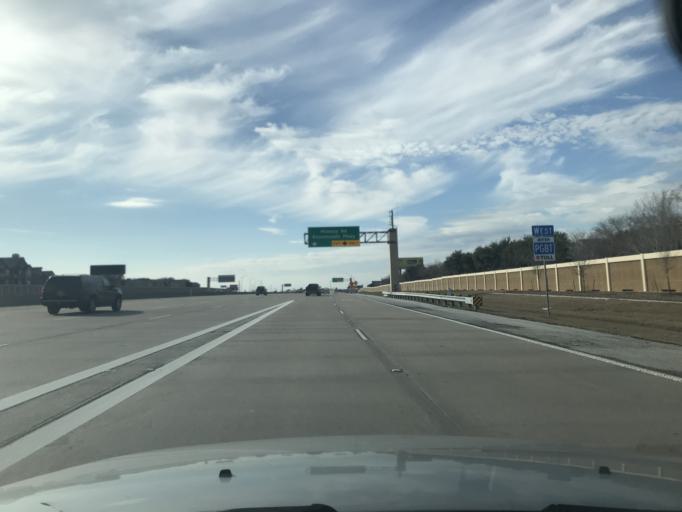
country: US
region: Texas
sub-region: Dallas County
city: Addison
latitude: 33.0130
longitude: -96.8345
